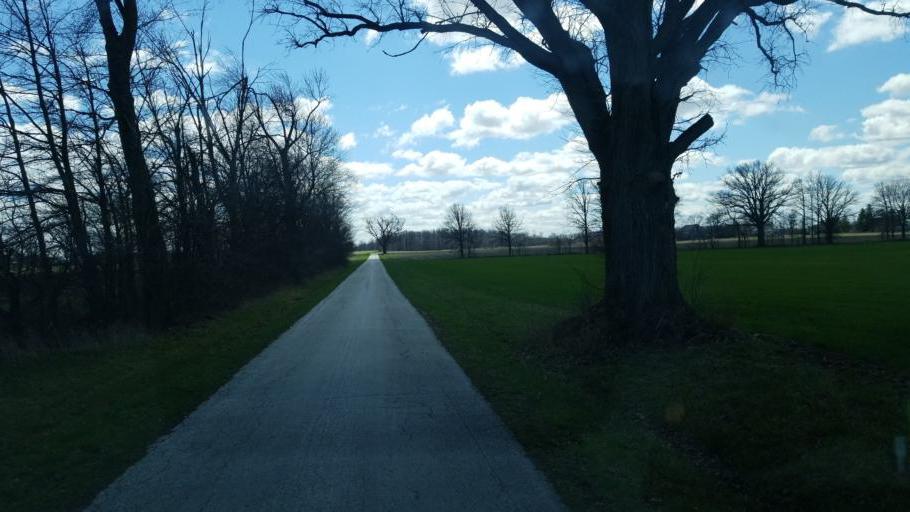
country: US
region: Ohio
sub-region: Hancock County
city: Arlington
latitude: 40.9502
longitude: -83.5229
